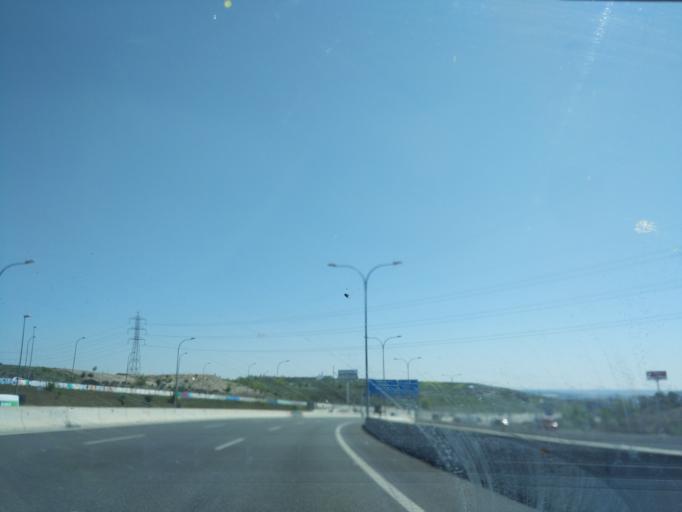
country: ES
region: Madrid
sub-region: Provincia de Madrid
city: Villa de Vallecas
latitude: 40.3671
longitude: -3.5800
